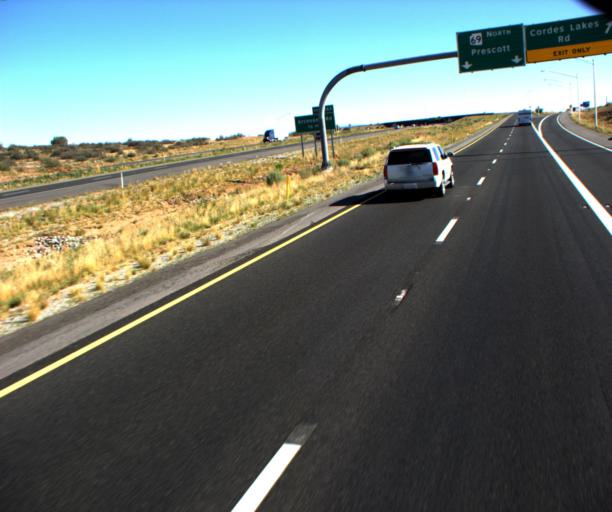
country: US
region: Arizona
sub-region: Yavapai County
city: Cordes Lakes
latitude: 34.3219
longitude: -112.1222
